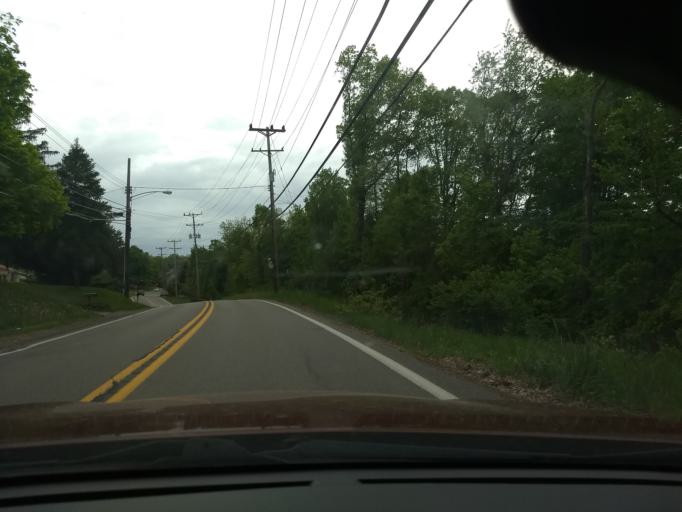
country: US
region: Pennsylvania
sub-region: Allegheny County
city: Coraopolis
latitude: 40.4904
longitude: -80.1357
